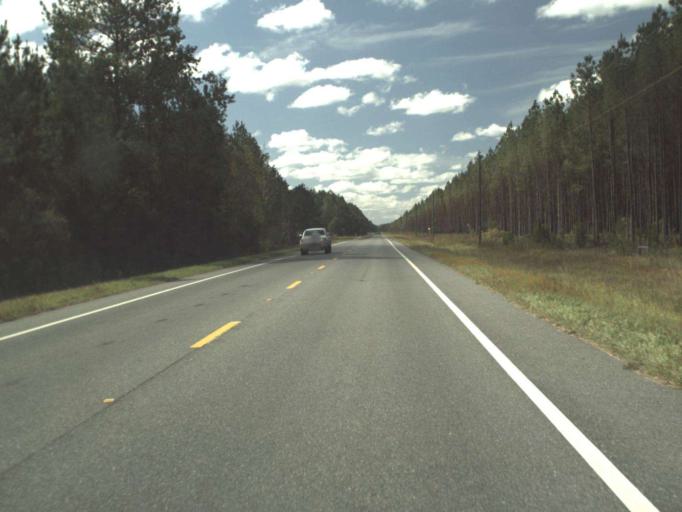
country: US
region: Florida
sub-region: Holmes County
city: Bonifay
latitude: 30.6600
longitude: -85.6547
